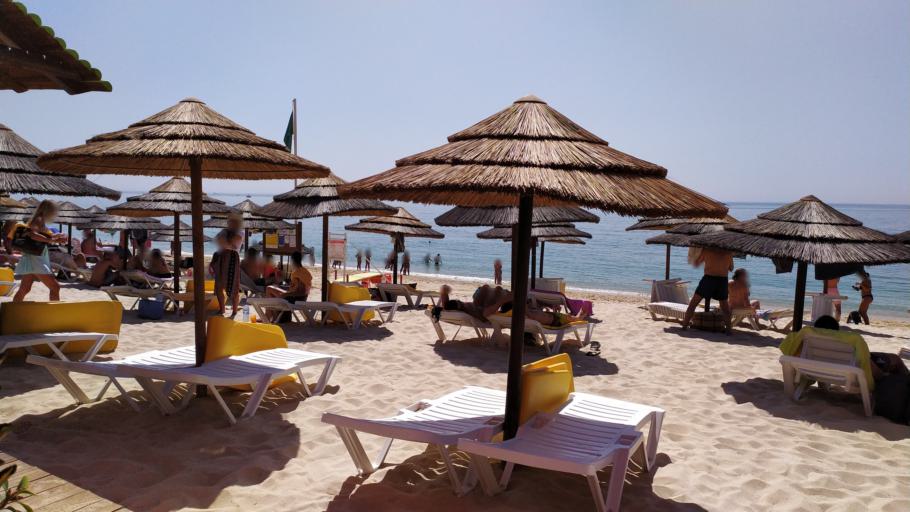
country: PT
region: Setubal
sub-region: Palmela
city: Quinta do Anjo
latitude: 38.4847
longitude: -8.9641
